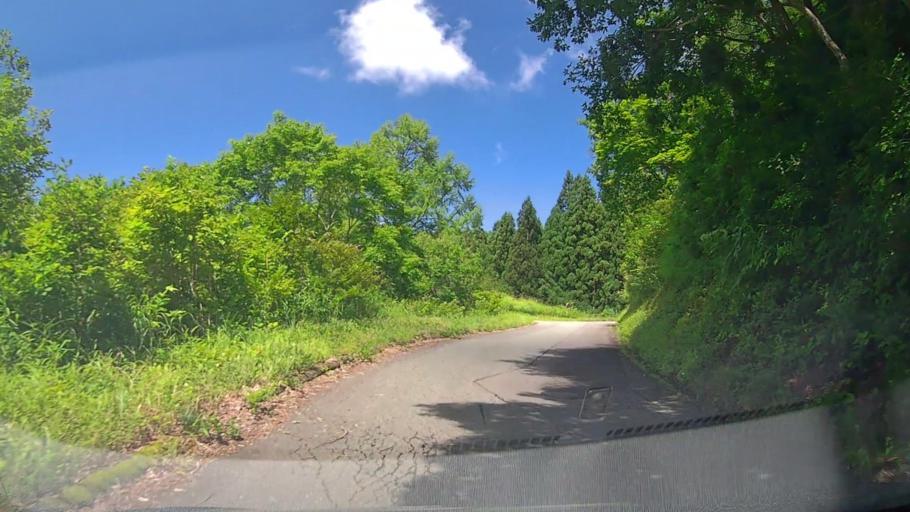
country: JP
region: Nagano
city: Iiyama
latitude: 36.9312
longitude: 138.4649
